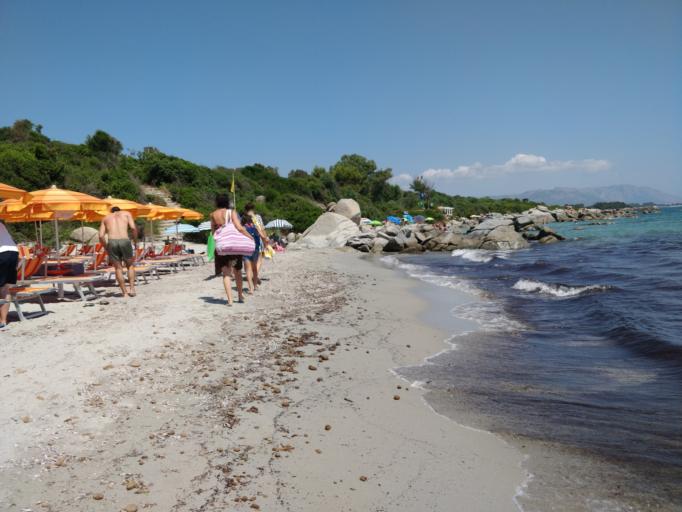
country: IT
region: Sardinia
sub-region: Provincia di Ogliastra
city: Tortoli
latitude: 39.8816
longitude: 9.6812
